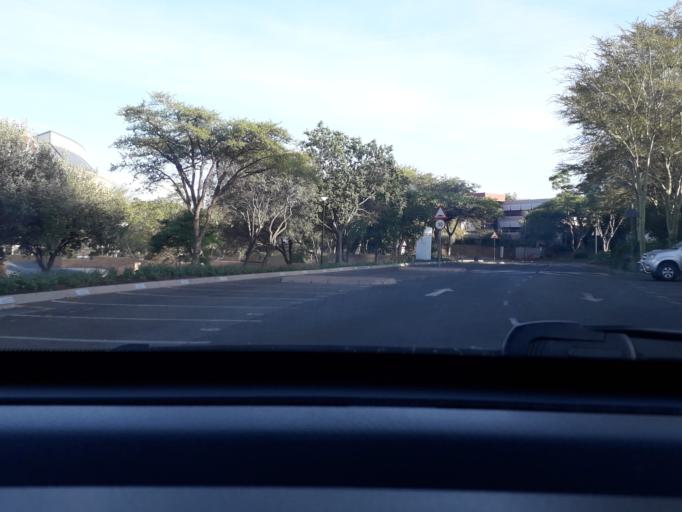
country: ZA
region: Gauteng
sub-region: City of Johannesburg Metropolitan Municipality
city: Midrand
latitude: -26.0598
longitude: 28.0881
